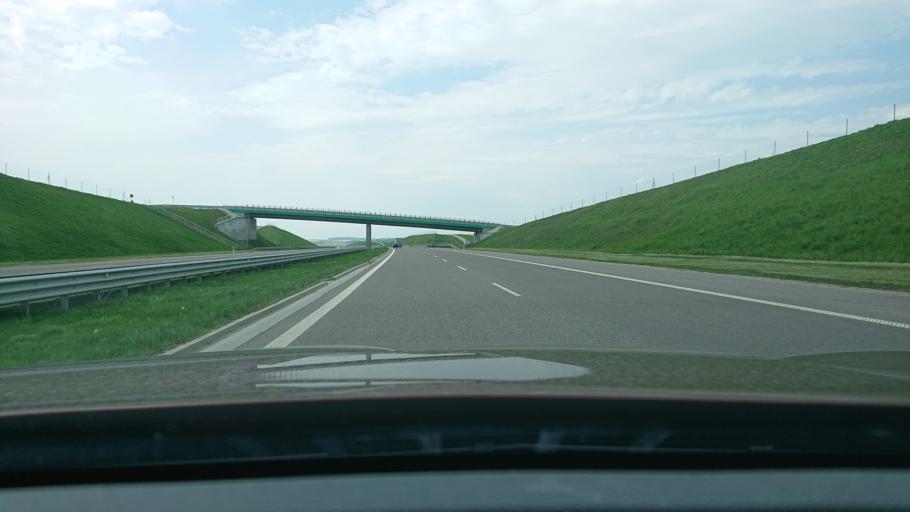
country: PL
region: Subcarpathian Voivodeship
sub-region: Powiat jaroslawski
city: Ostrow
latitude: 49.9299
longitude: 22.7176
